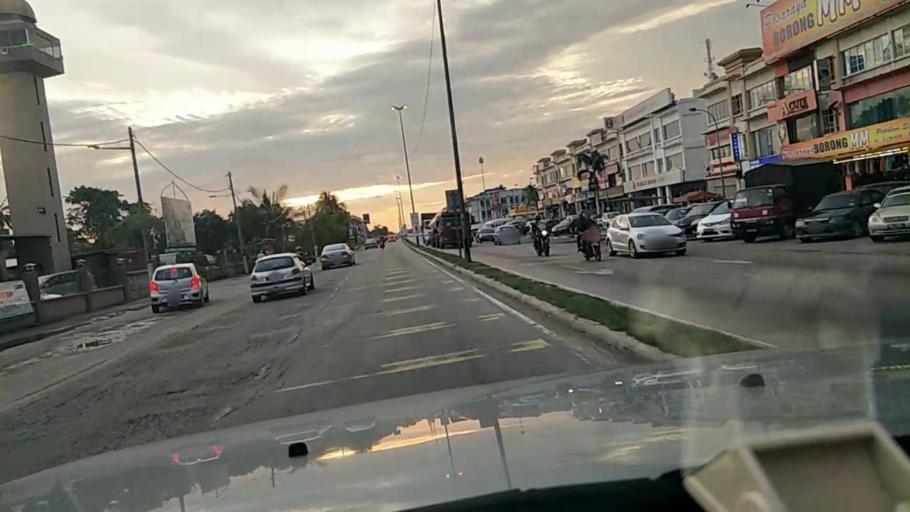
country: MY
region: Perak
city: Kampong Dungun
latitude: 3.1384
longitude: 101.3708
